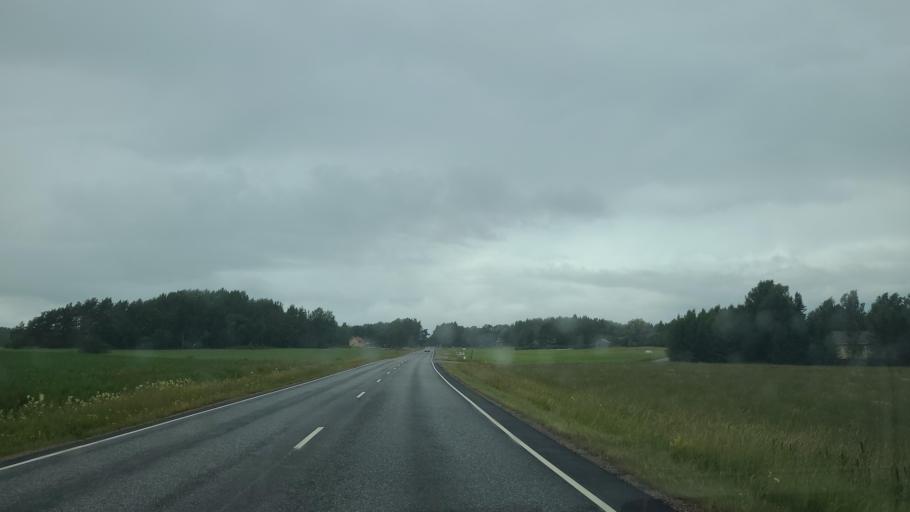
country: FI
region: Varsinais-Suomi
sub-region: Aboland-Turunmaa
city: Kimito
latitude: 60.1858
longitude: 22.7144
